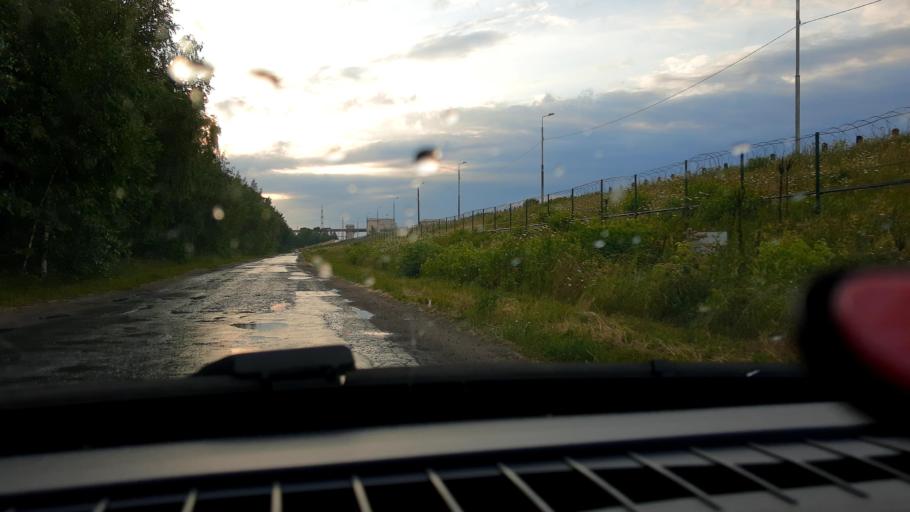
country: RU
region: Nizjnij Novgorod
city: Zavolzh'ye
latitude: 56.6717
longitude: 43.4243
